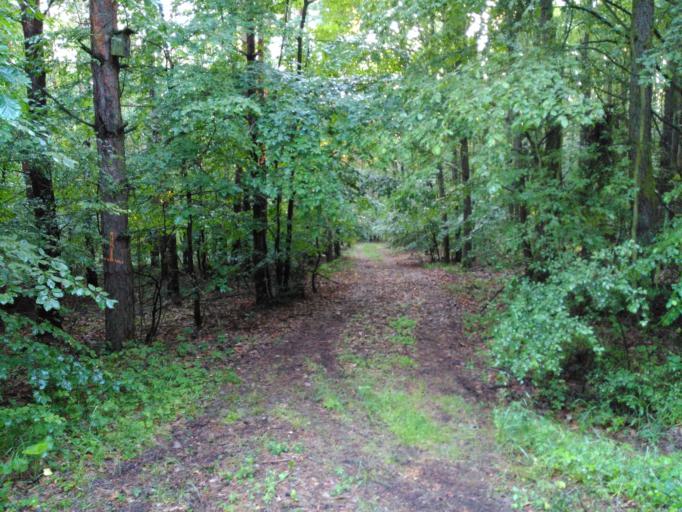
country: CZ
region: Central Bohemia
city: Hudlice
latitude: 49.9587
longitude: 13.9237
